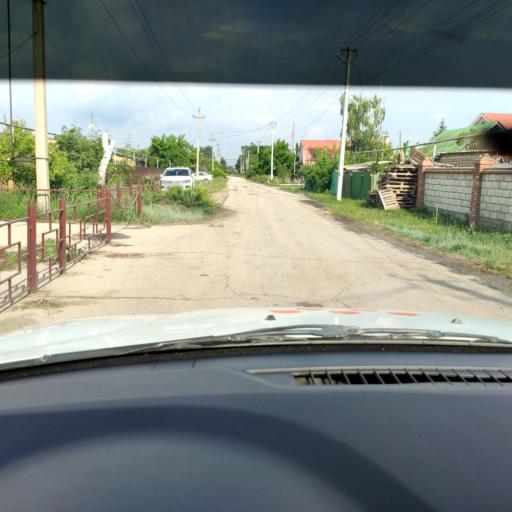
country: RU
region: Samara
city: Podstepki
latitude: 53.6141
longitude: 49.0356
